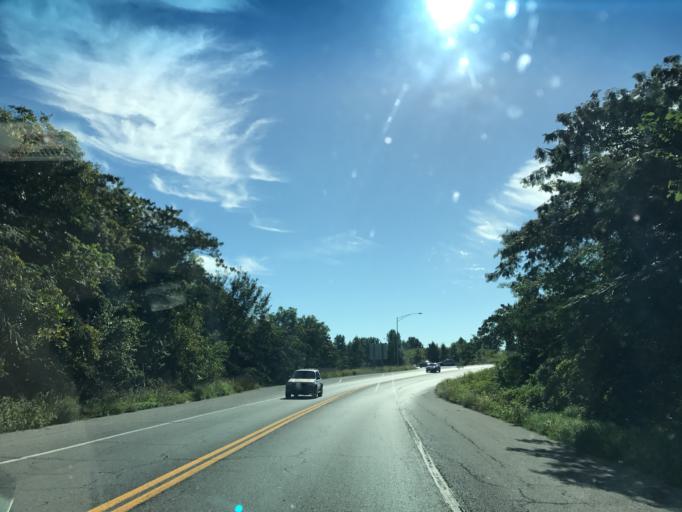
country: US
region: Maryland
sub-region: Anne Arundel County
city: Davidsonville
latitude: 38.9554
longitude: -76.6439
